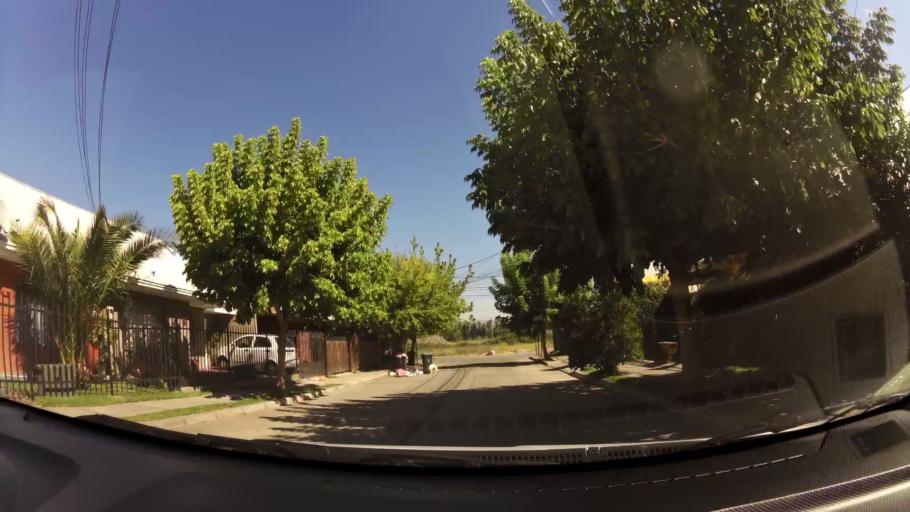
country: CL
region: Maule
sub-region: Provincia de Curico
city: Curico
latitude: -34.9686
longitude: -71.2549
